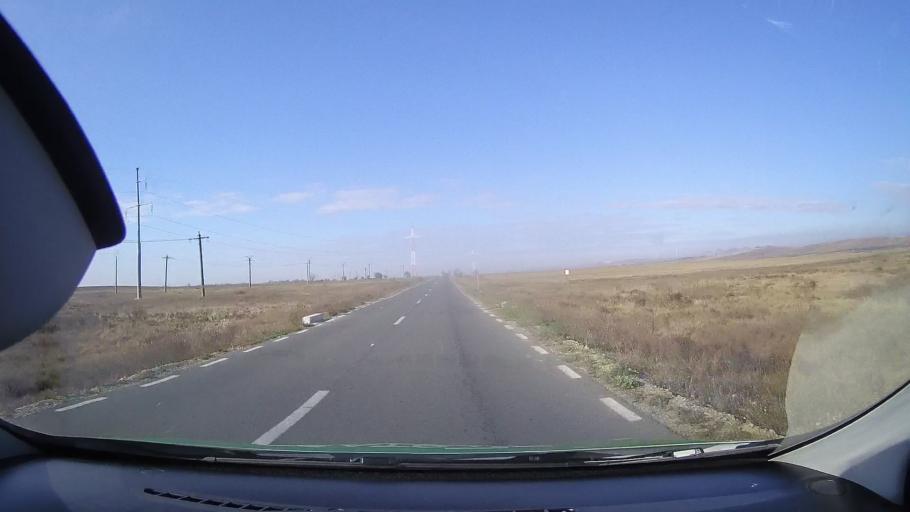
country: RO
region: Tulcea
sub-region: Comuna Murighiol
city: Murighiol
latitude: 45.0281
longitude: 29.1525
